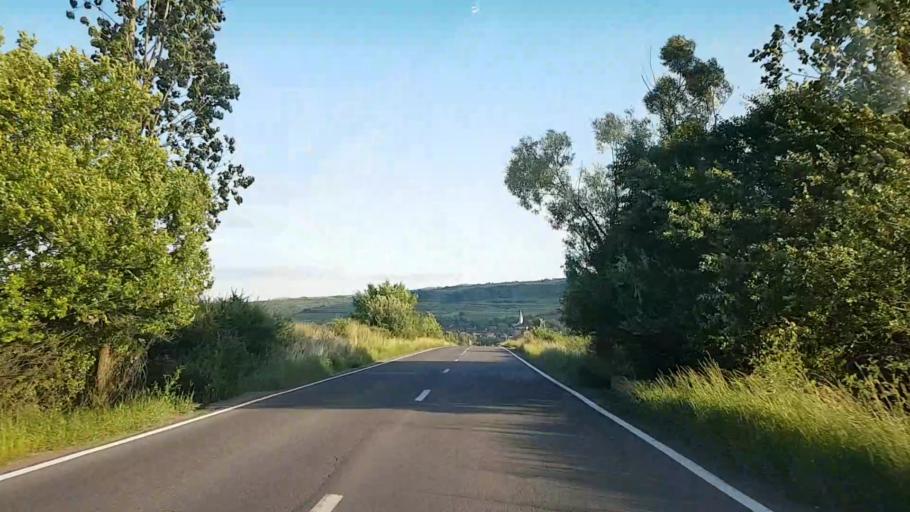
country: RO
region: Harghita
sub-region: Comuna Praid
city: Praid
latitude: 46.5399
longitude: 25.1308
